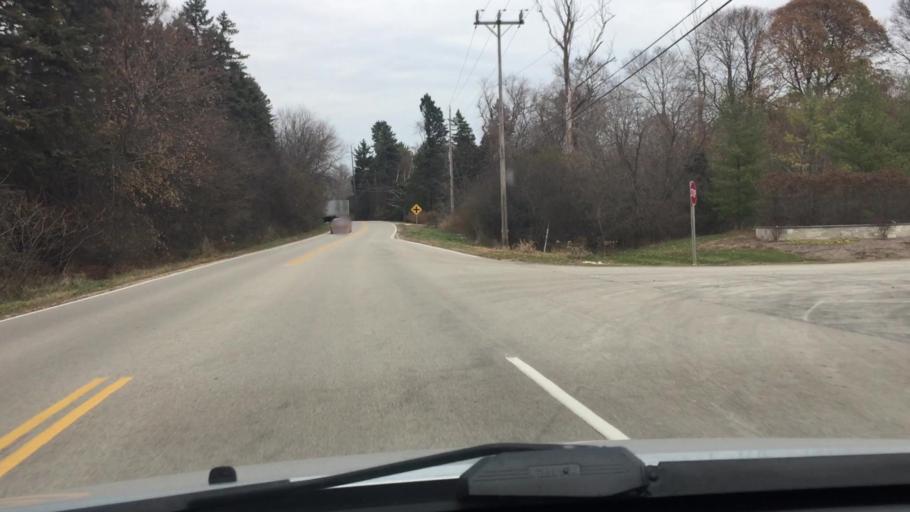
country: US
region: Wisconsin
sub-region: Ozaukee County
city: Thiensville
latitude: 43.2630
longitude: -87.9768
